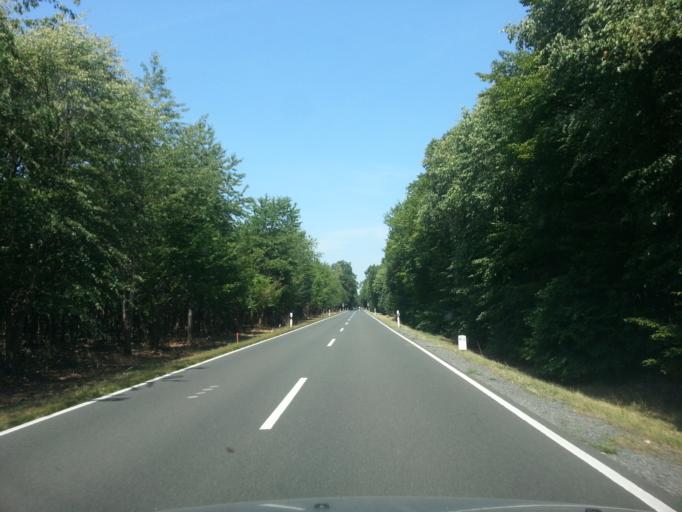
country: DE
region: Hesse
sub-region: Regierungsbezirk Darmstadt
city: Einhausen
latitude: 49.6977
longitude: 8.5191
